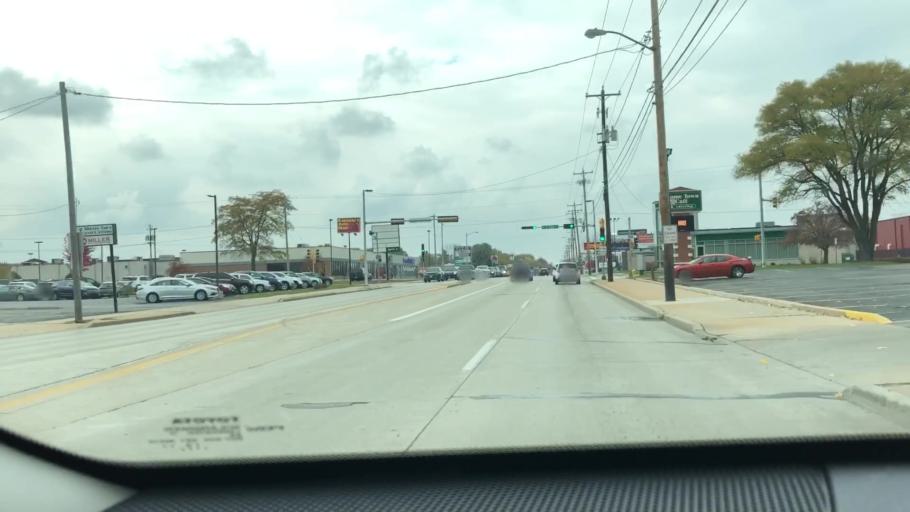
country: US
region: Wisconsin
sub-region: Brown County
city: Howard
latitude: 44.5219
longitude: -88.0588
